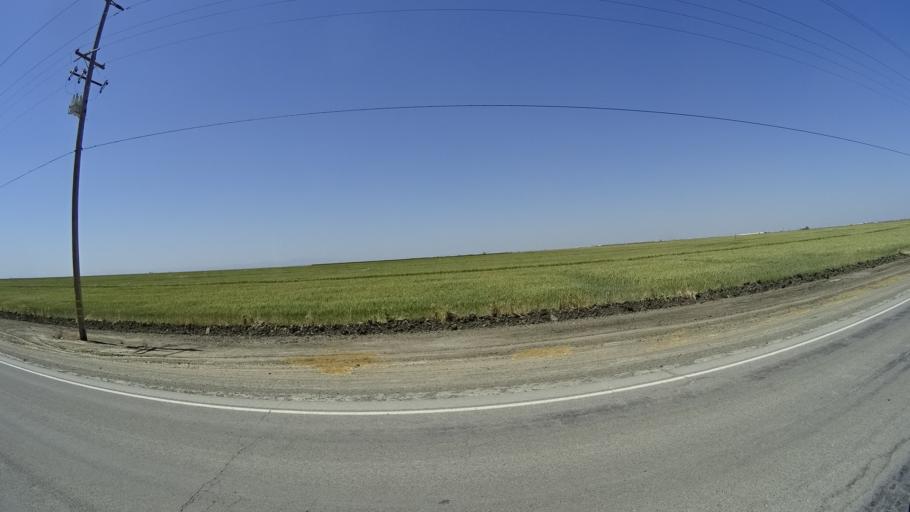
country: US
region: California
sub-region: Kings County
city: Corcoran
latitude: 36.1293
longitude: -119.6444
